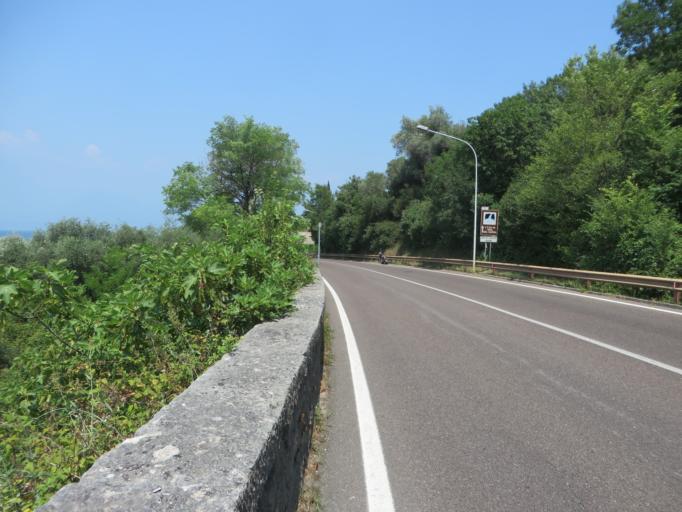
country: IT
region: Veneto
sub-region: Provincia di Verona
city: Torri del Benaco
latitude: 45.5826
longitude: 10.6744
